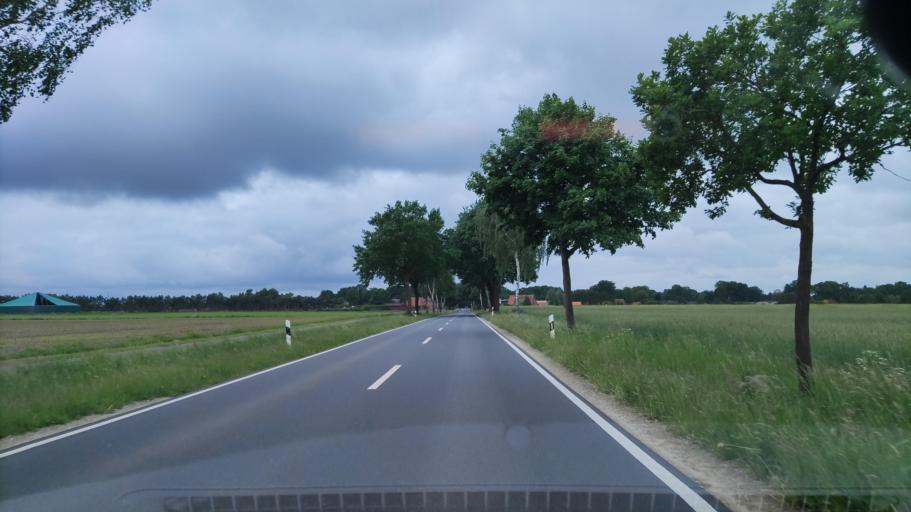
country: DE
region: Lower Saxony
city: Fintel
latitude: 53.1034
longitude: 9.6825
